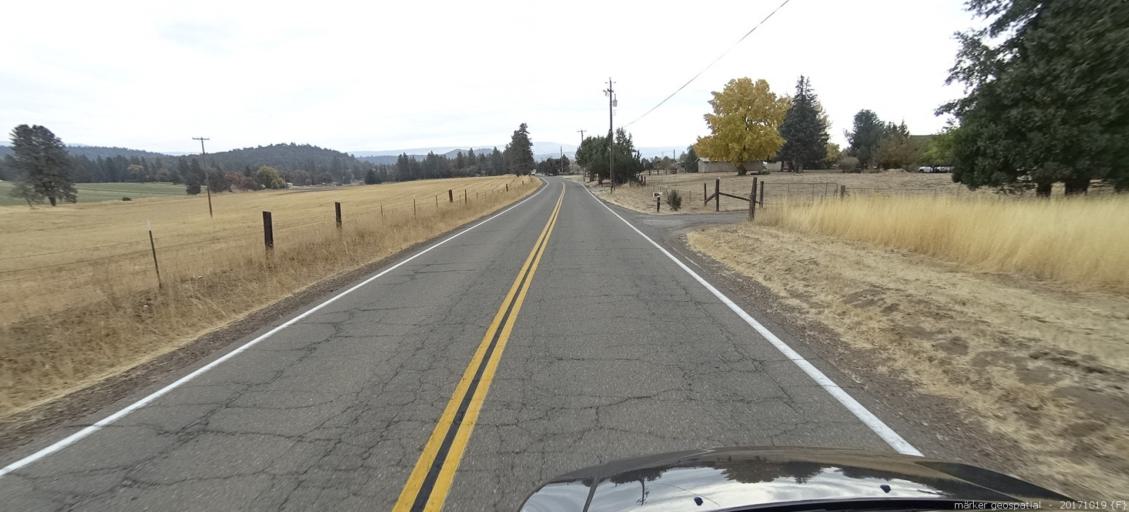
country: US
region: California
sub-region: Shasta County
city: Burney
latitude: 41.0513
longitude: -121.3472
